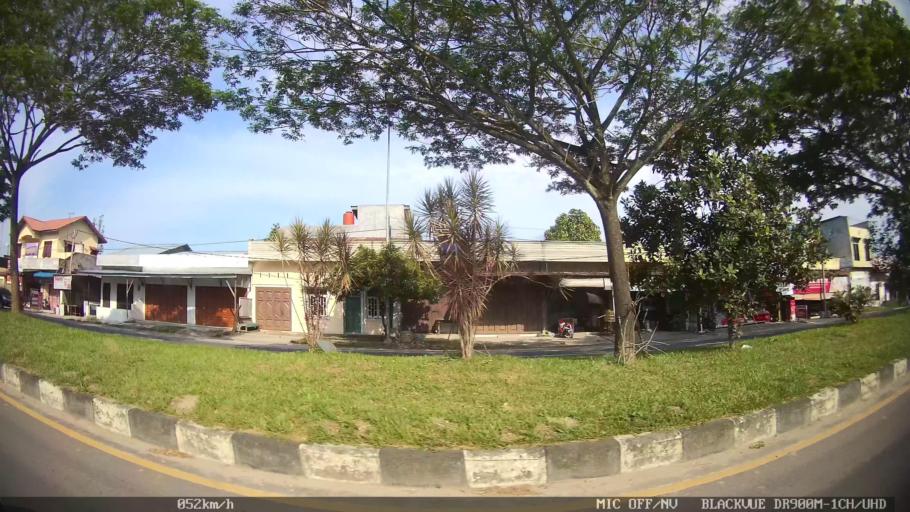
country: ID
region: North Sumatra
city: Percut
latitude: 3.5897
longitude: 98.8052
